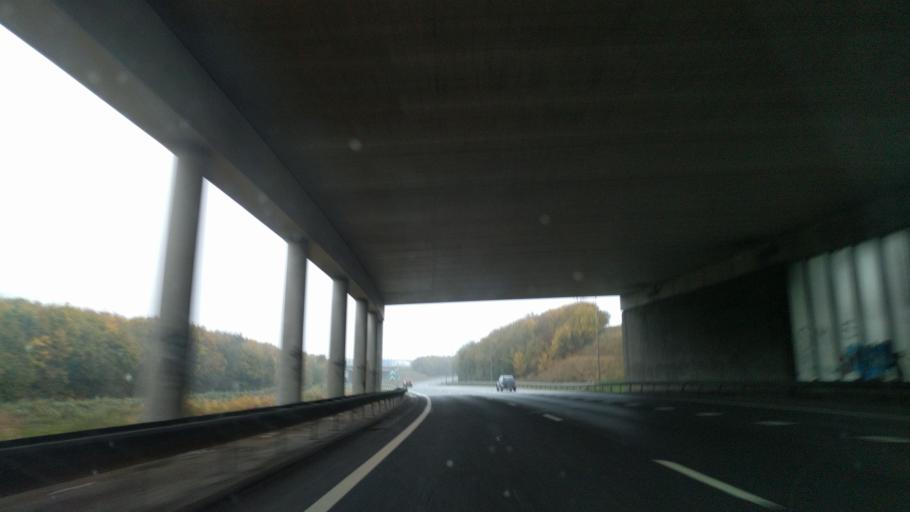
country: NL
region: South Holland
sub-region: Gemeente Barendrecht
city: Barendrecht
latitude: 51.8699
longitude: 4.5618
